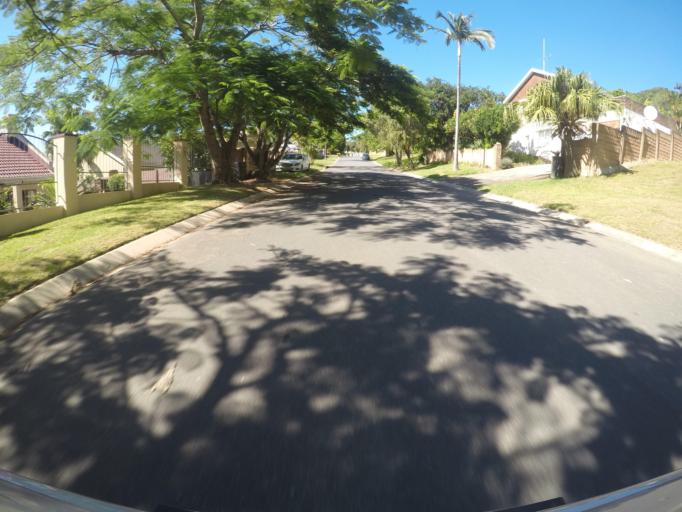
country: ZA
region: Eastern Cape
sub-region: Buffalo City Metropolitan Municipality
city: East London
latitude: -32.9521
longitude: 27.9008
